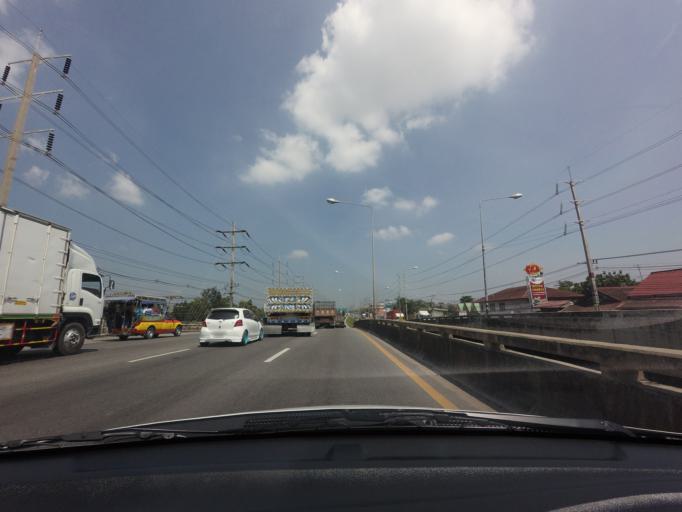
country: TH
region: Chachoengsao
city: Chachoengsao
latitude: 13.6555
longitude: 101.0476
